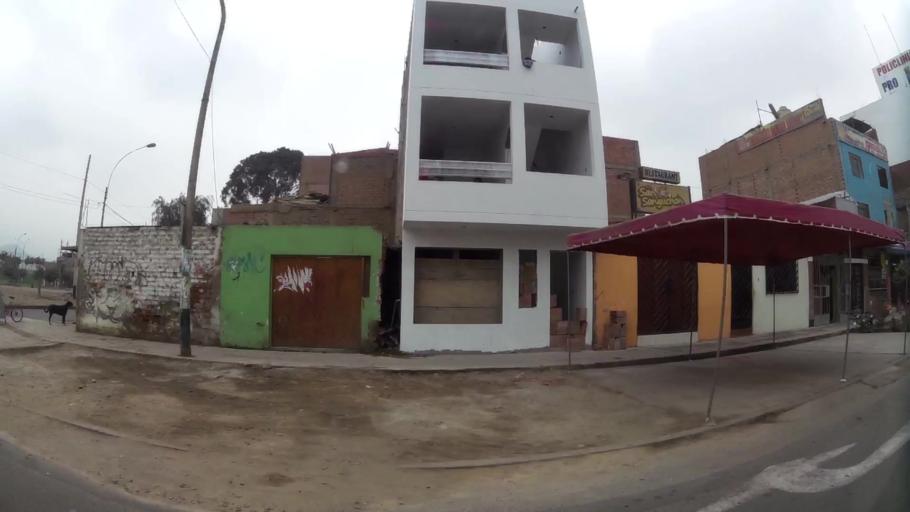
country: PE
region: Lima
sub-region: Lima
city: Independencia
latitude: -11.9330
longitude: -77.0801
